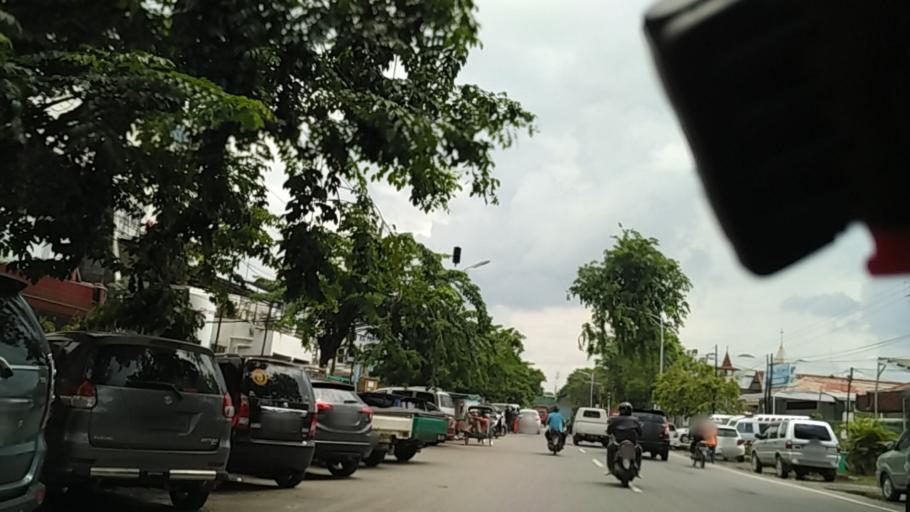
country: ID
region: Central Java
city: Semarang
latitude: -6.9727
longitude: 110.4342
